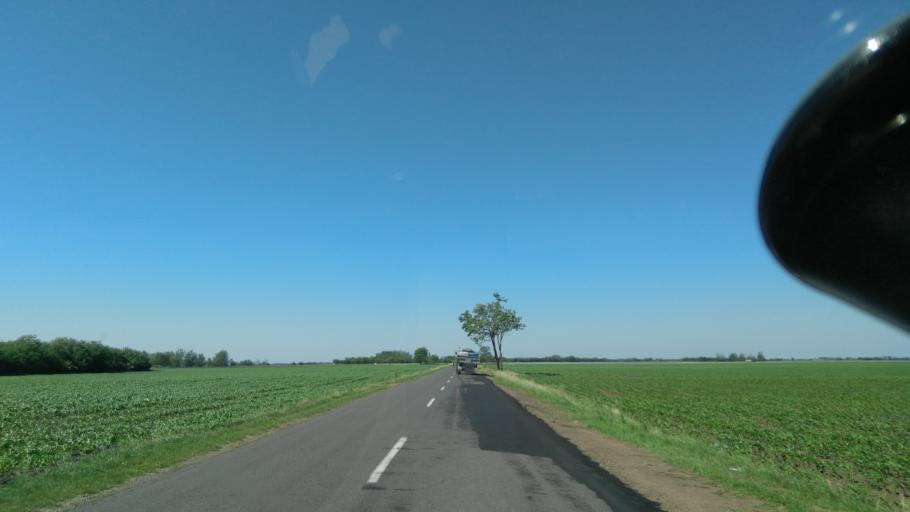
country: HU
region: Bekes
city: Kevermes
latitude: 46.4347
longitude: 21.1731
